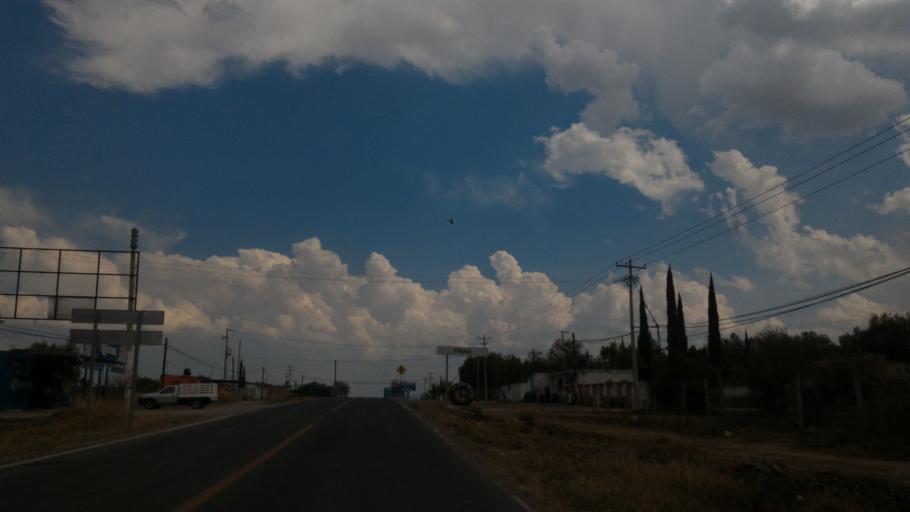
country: MX
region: Guanajuato
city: Ciudad Manuel Doblado
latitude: 20.8040
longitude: -101.9947
